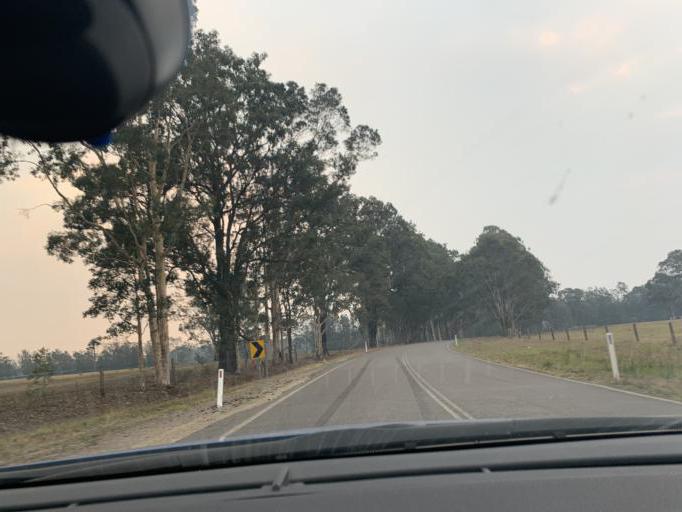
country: AU
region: New South Wales
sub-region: Cessnock
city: Cessnock
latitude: -32.9290
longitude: 151.3262
